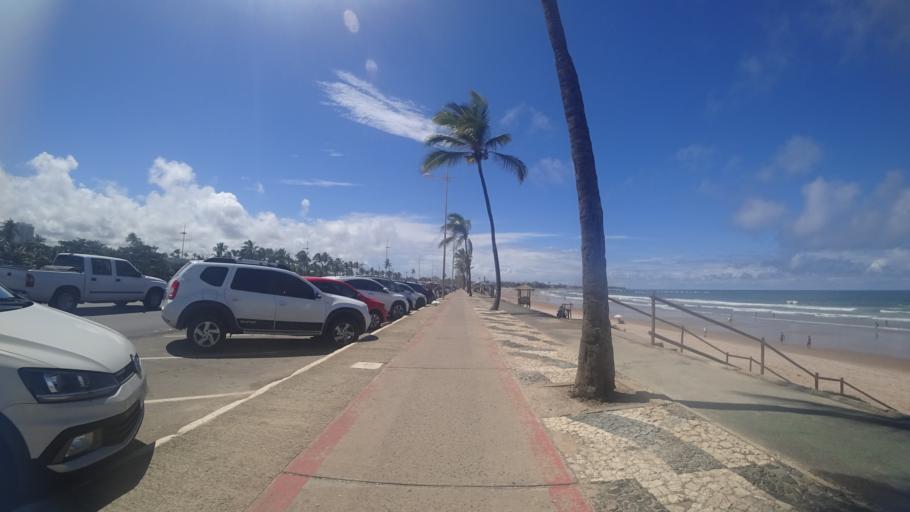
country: BR
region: Bahia
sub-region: Lauro De Freitas
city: Lauro de Freitas
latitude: -12.9574
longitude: -38.3899
